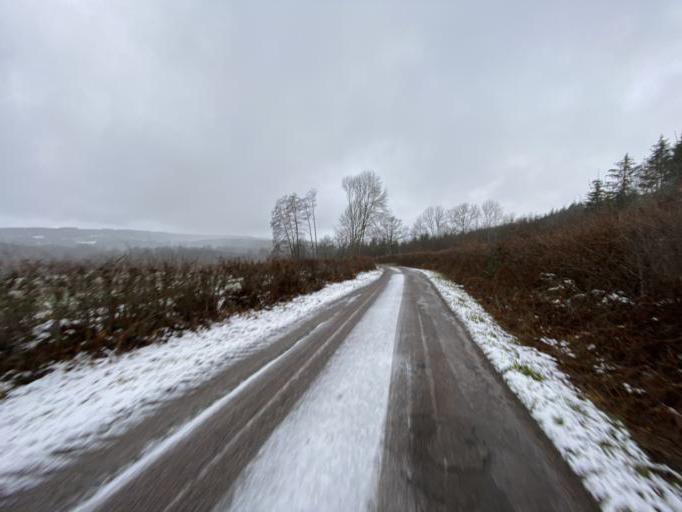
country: FR
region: Bourgogne
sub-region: Departement de la Cote-d'Or
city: Saulieu
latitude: 47.2670
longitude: 4.1595
